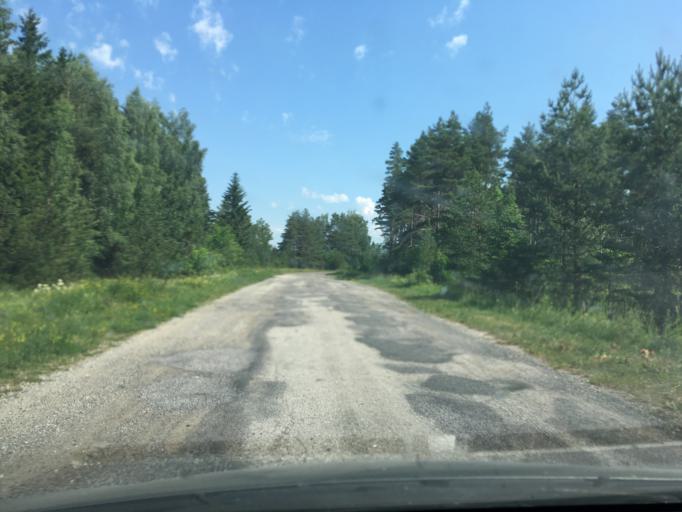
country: EE
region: Laeaene
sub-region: Lihula vald
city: Lihula
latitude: 58.6644
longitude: 23.7413
